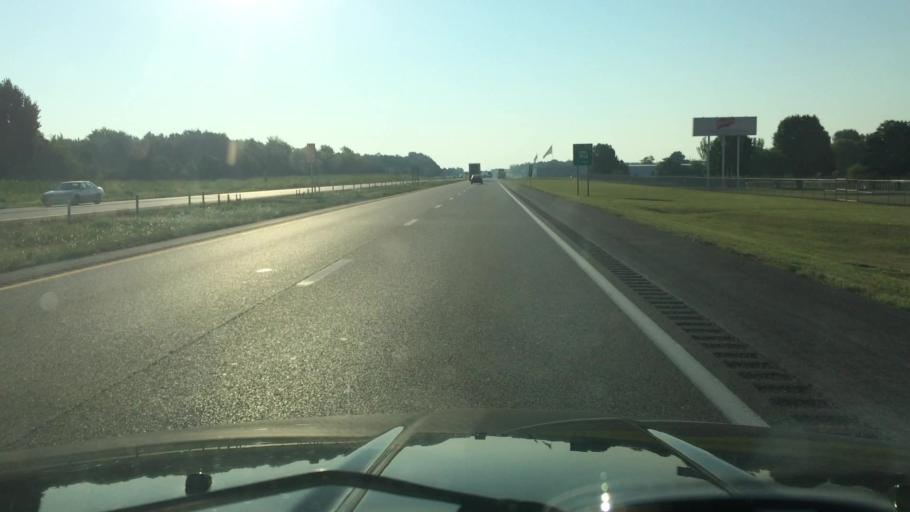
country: US
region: Missouri
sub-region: Greene County
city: Strafford
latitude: 37.2501
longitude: -93.2060
